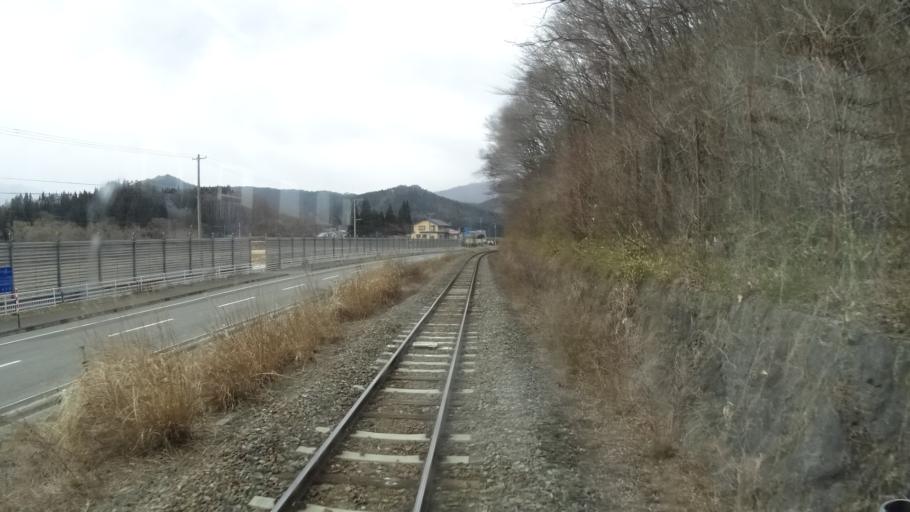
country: JP
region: Iwate
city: Tono
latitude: 39.3019
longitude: 141.4070
